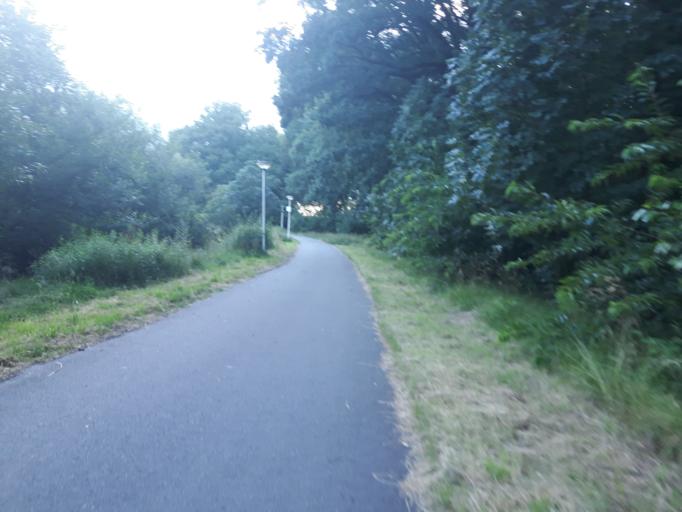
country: NL
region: Overijssel
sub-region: Gemeente Enschede
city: Enschede
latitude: 52.2029
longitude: 6.8724
